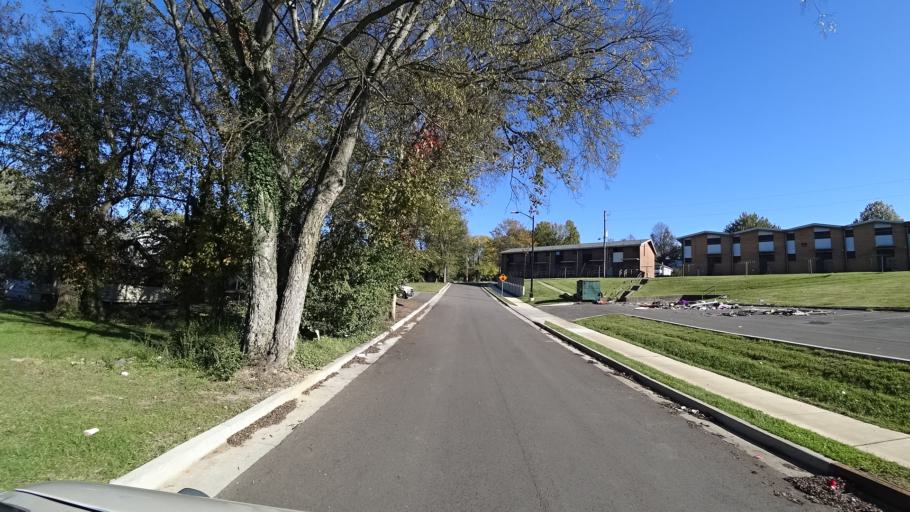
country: US
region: Tennessee
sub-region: Knox County
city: Knoxville
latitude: 35.9788
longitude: -83.8928
